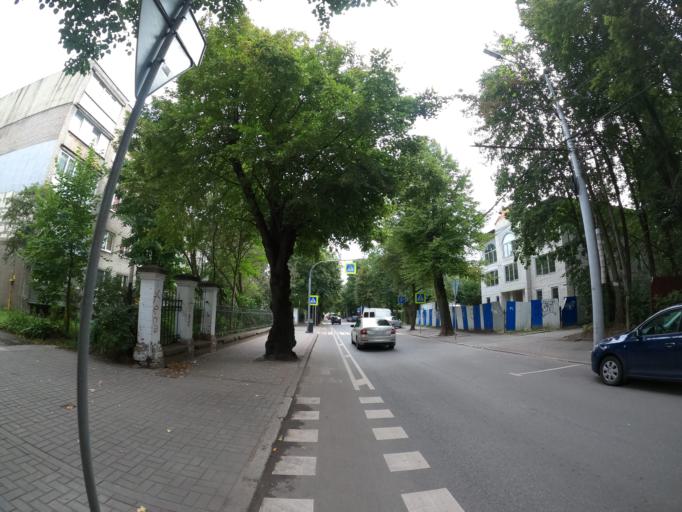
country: RU
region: Kaliningrad
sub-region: Gorod Kaliningrad
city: Kaliningrad
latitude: 54.7244
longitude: 20.4789
